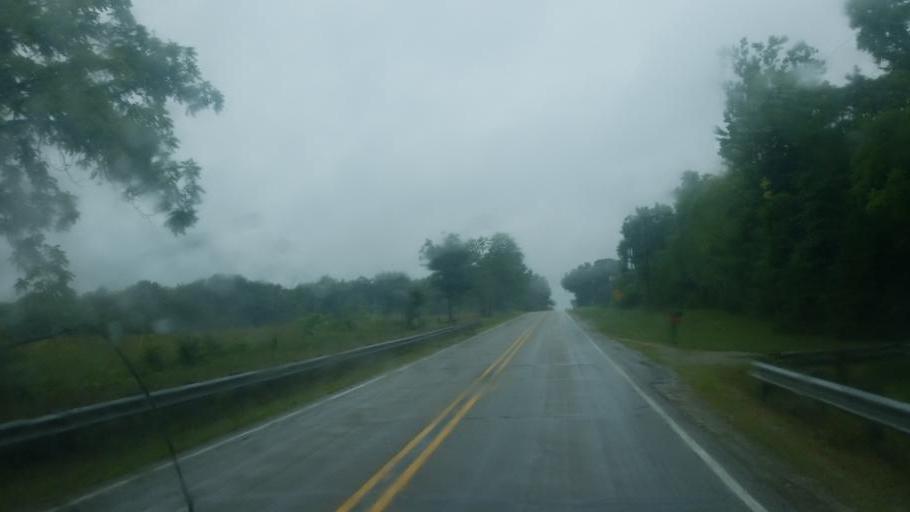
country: US
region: Indiana
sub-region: Huntington County
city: Warren
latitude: 40.6653
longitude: -85.4086
